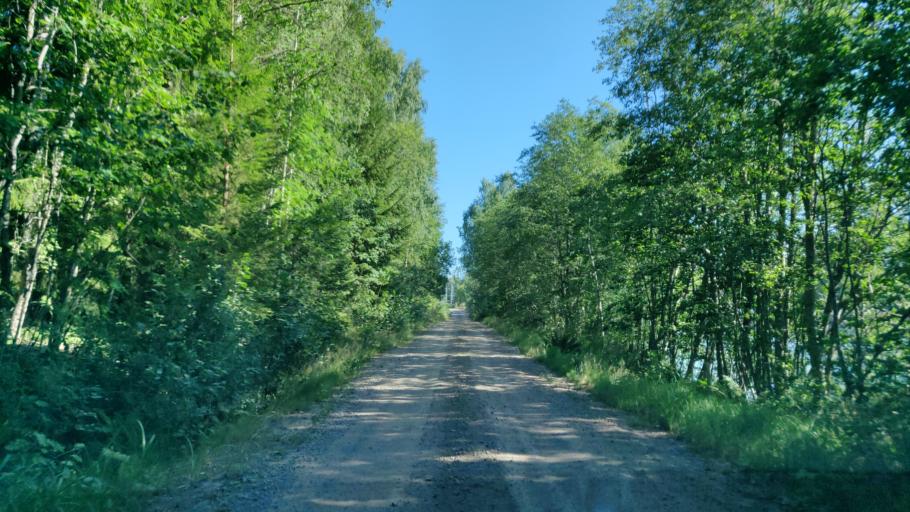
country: SE
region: Vaermland
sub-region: Hagfors Kommun
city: Ekshaerad
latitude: 60.0468
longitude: 13.5260
